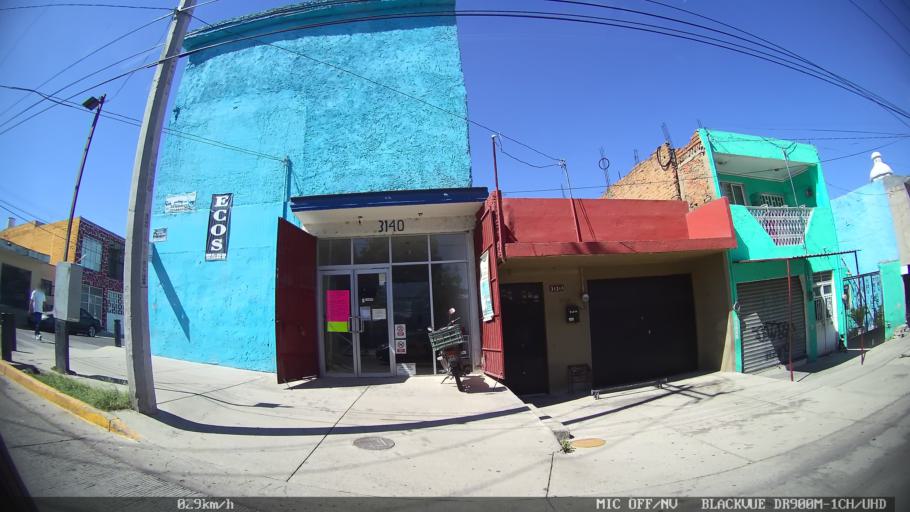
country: MX
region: Jalisco
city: Tlaquepaque
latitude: 20.6953
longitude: -103.2848
